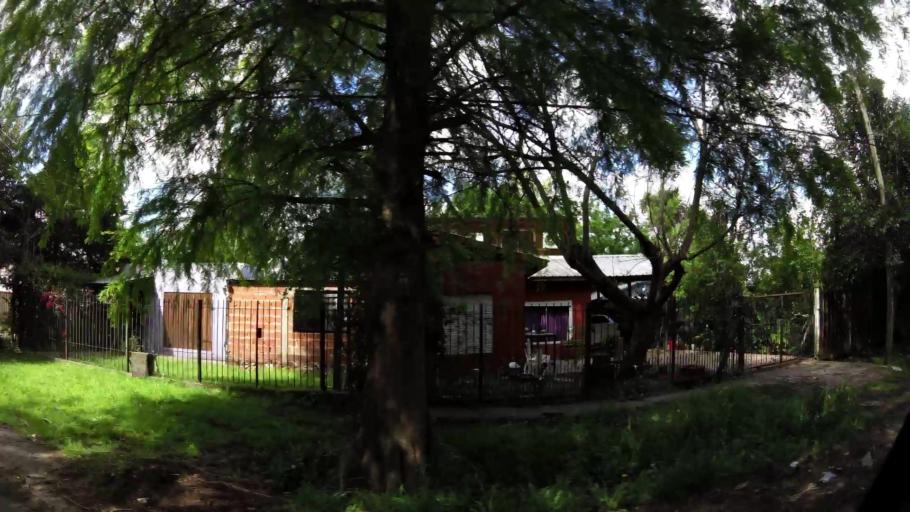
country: AR
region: Buenos Aires
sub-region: Partido de Quilmes
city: Quilmes
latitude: -34.8363
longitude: -58.1703
